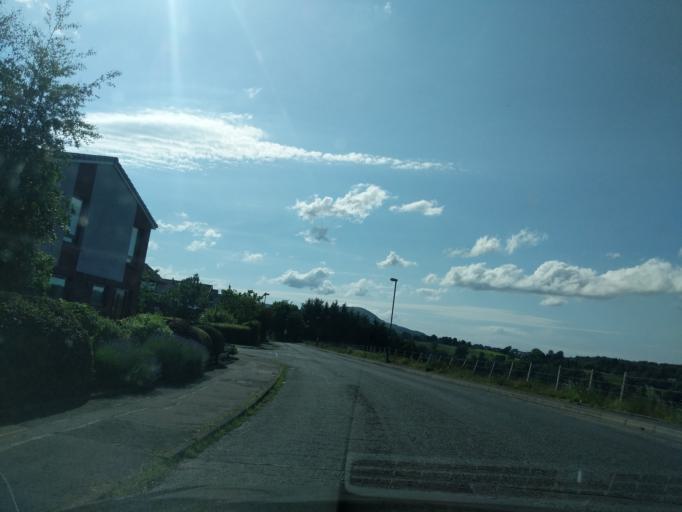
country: GB
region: Scotland
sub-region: Midlothian
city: Bonnyrigg
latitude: 55.8724
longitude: -3.1274
